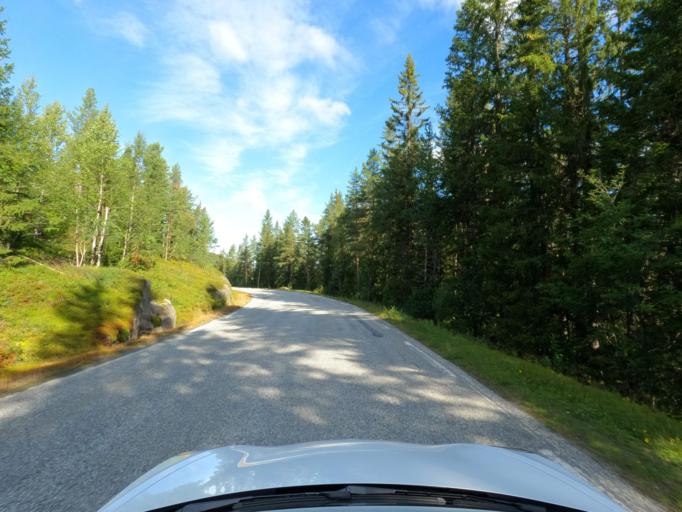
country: NO
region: Telemark
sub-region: Tinn
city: Rjukan
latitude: 59.9605
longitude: 8.8867
